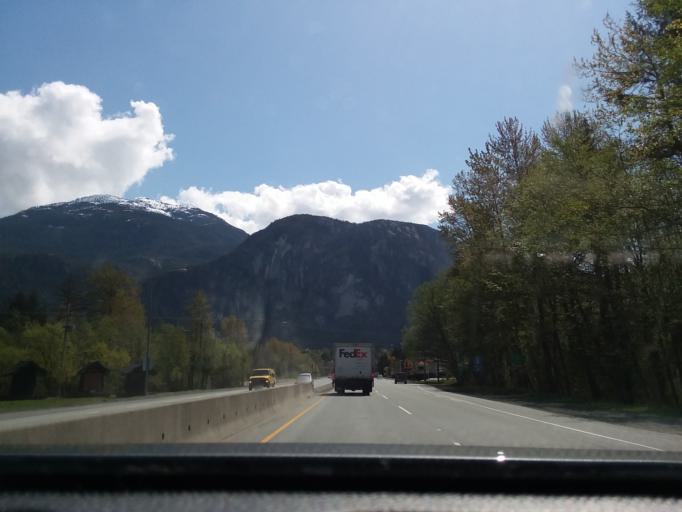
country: CA
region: British Columbia
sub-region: Greater Vancouver Regional District
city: Lions Bay
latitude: 49.7070
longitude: -123.1466
